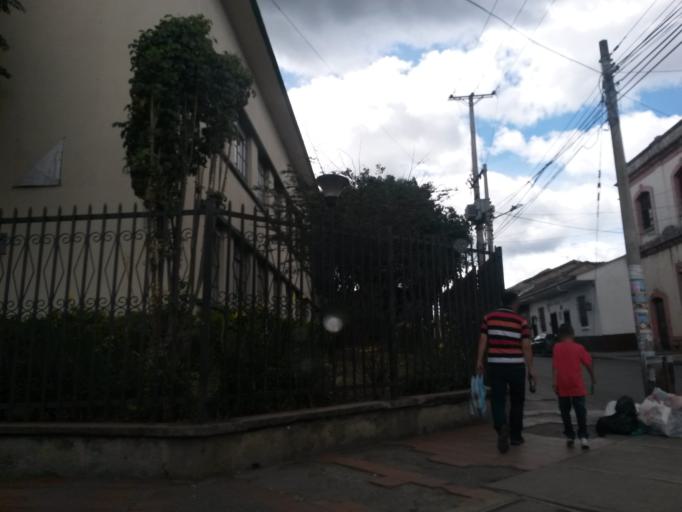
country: CO
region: Cauca
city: Popayan
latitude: 2.4387
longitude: -76.6041
